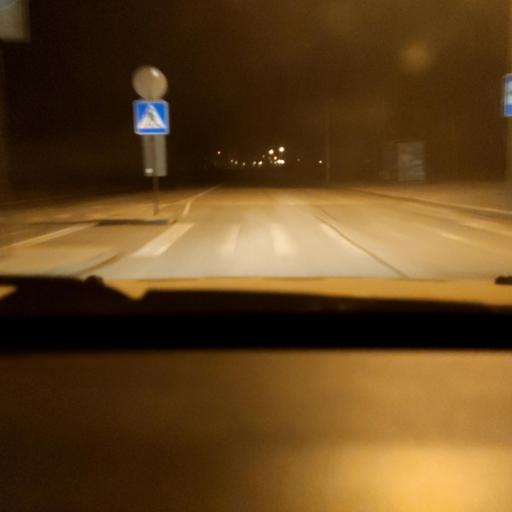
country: RU
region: Perm
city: Polazna
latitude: 58.1204
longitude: 56.4033
